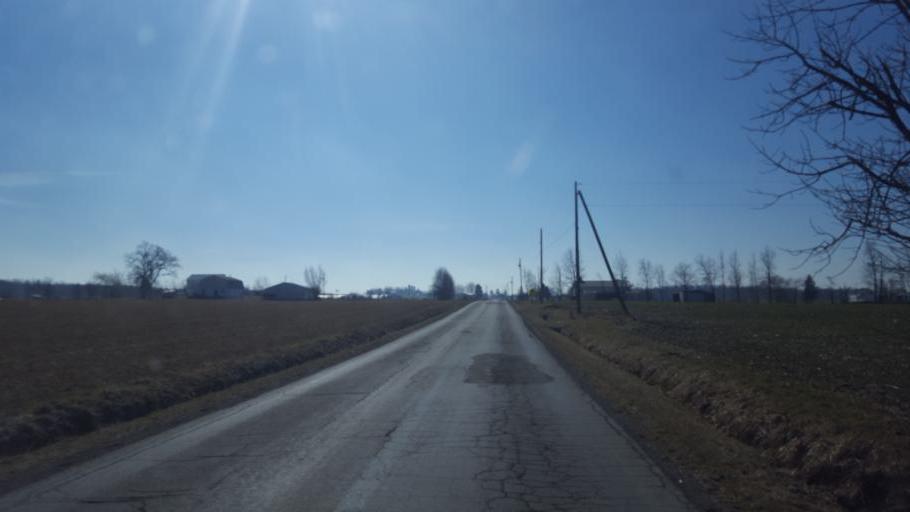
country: US
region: Ohio
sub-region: Huron County
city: Greenwich
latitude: 40.9910
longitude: -82.5821
